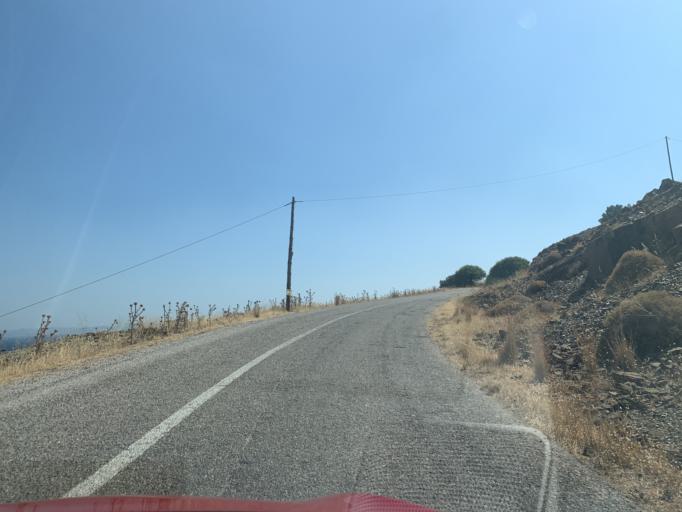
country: GR
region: North Aegean
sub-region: Chios
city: Vrontados
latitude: 38.4803
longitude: 25.8941
